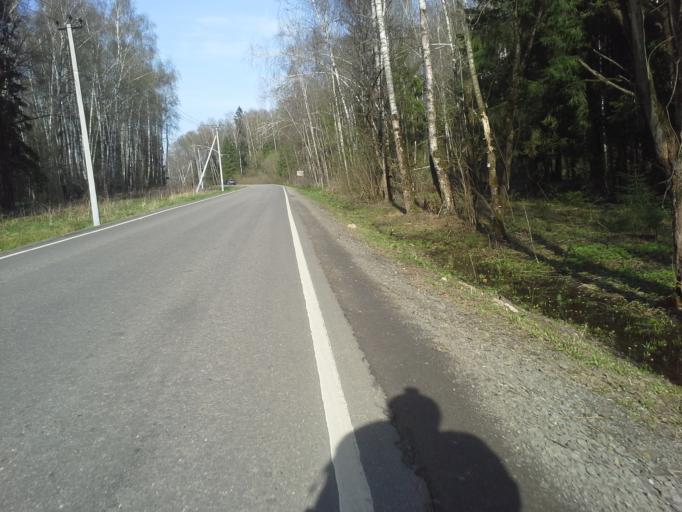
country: RU
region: Moskovskaya
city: Vatutinki
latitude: 55.4706
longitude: 37.3846
